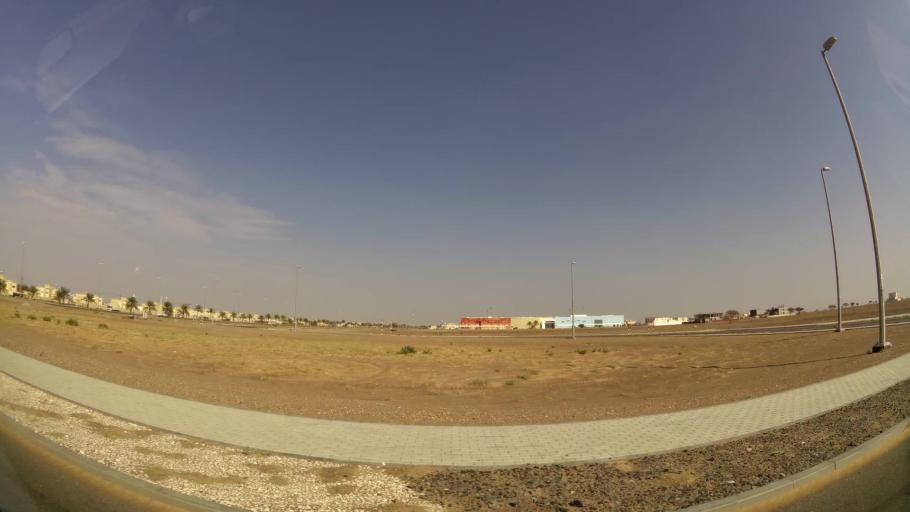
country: AE
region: Abu Dhabi
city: Al Ain
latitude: 24.0921
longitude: 55.8917
